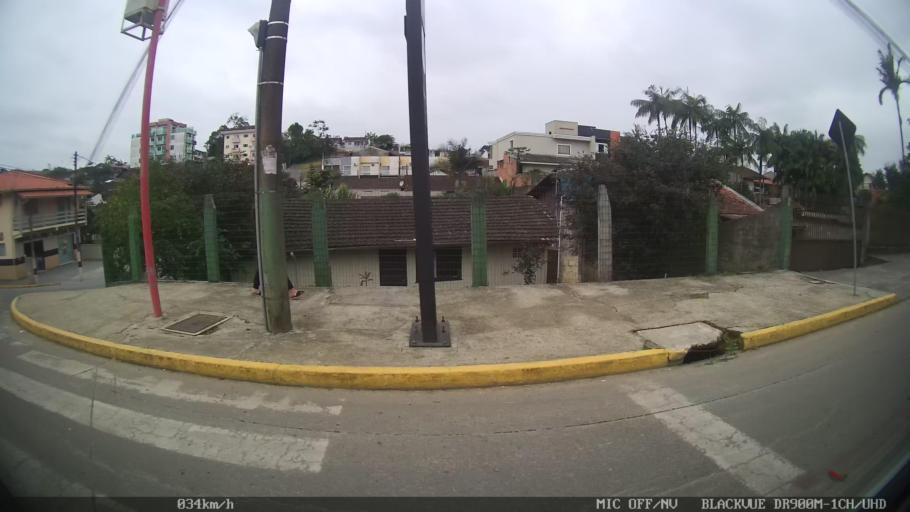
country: BR
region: Santa Catarina
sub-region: Joinville
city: Joinville
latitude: -26.3552
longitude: -48.8388
